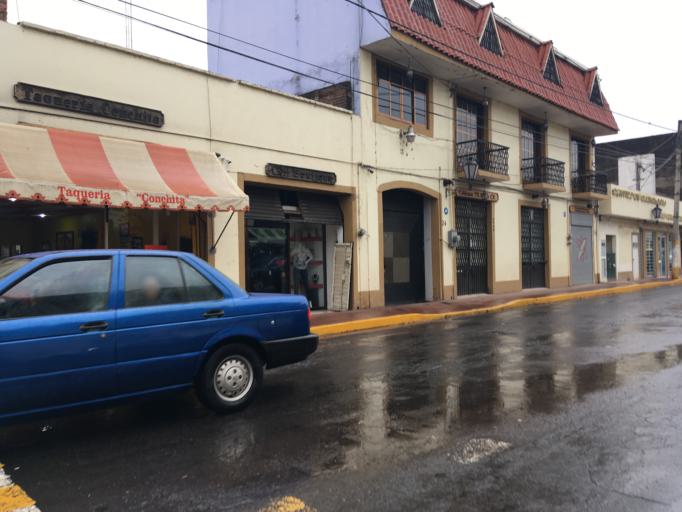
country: MX
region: Puebla
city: Chignahuapan
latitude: 19.8397
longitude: -98.0321
